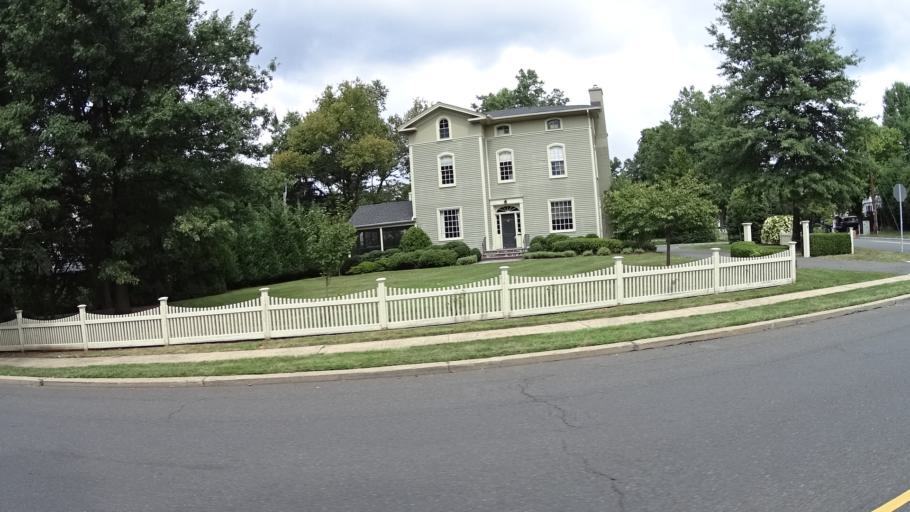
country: US
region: New Jersey
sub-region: Morris County
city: Chatham
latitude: 40.7132
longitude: -74.3742
